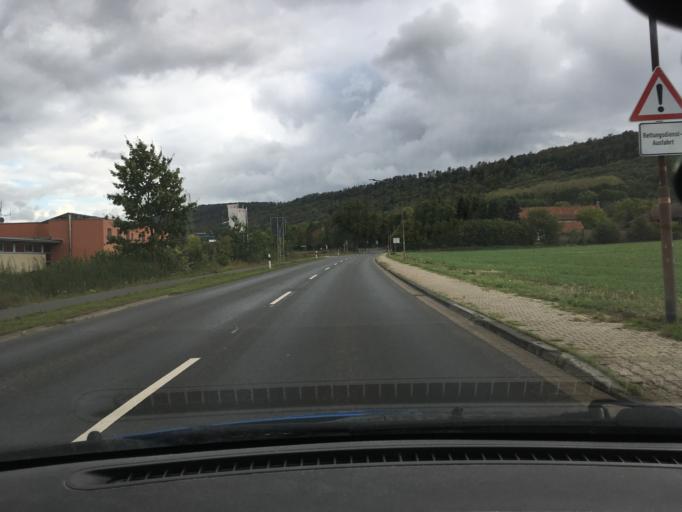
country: DE
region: Lower Saxony
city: Springe
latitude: 52.2008
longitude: 9.5570
